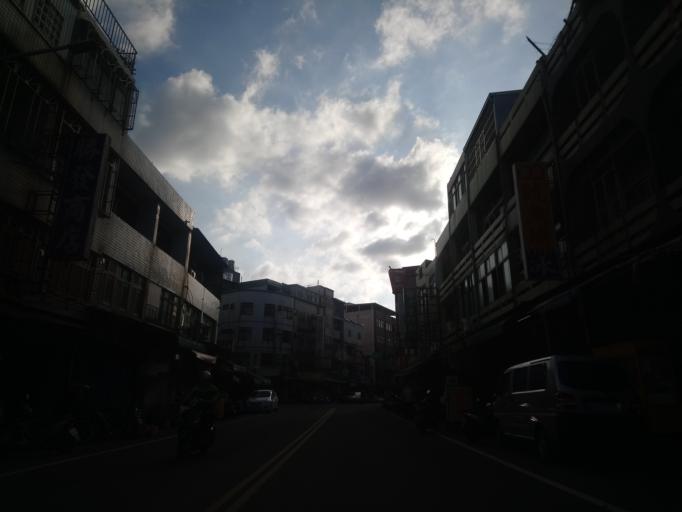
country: TW
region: Taiwan
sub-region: Hsinchu
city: Hsinchu
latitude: 24.7969
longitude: 120.9419
